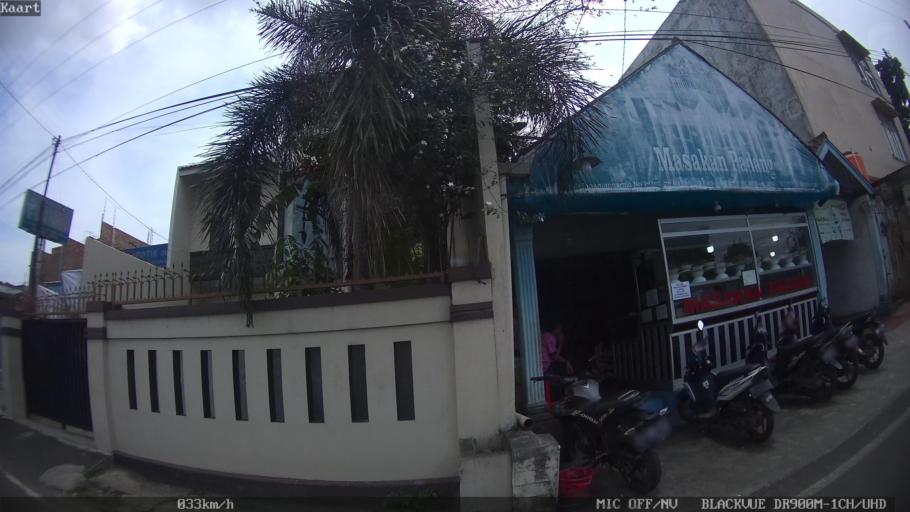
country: ID
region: Lampung
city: Kedaton
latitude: -5.4001
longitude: 105.2445
